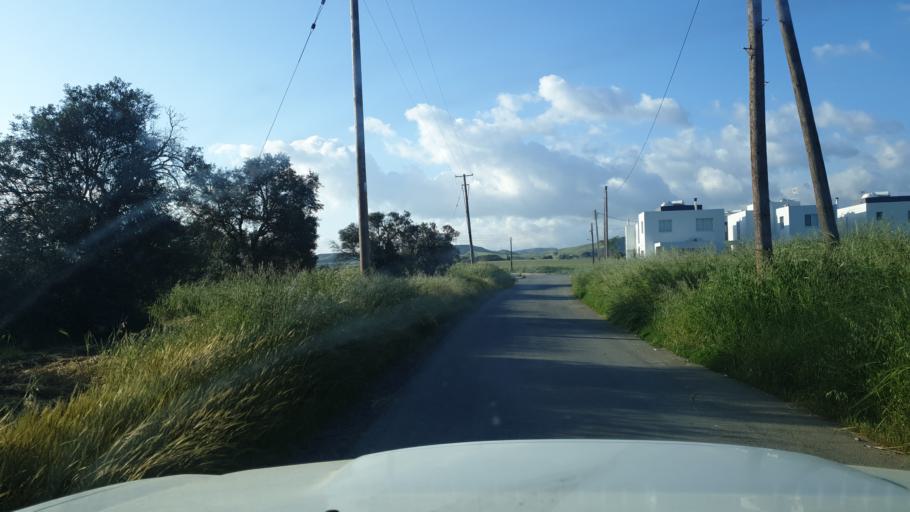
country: CY
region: Lefkosia
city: Tseri
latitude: 35.0614
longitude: 33.3290
